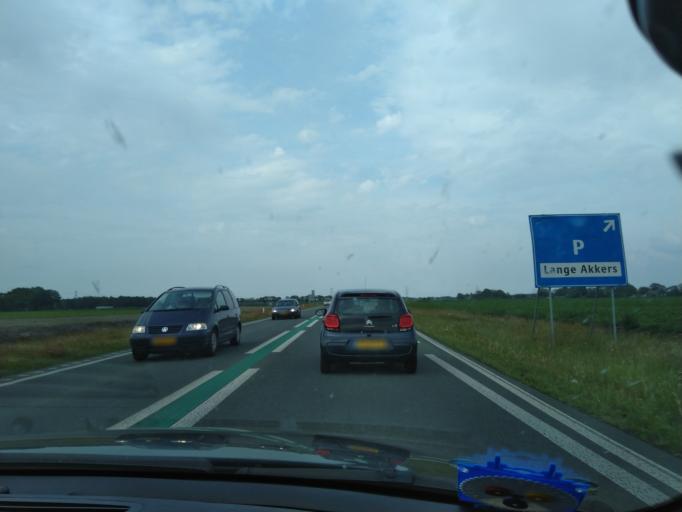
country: NL
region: Drenthe
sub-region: Gemeente Coevorden
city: Dalen
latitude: 52.7142
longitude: 6.7626
